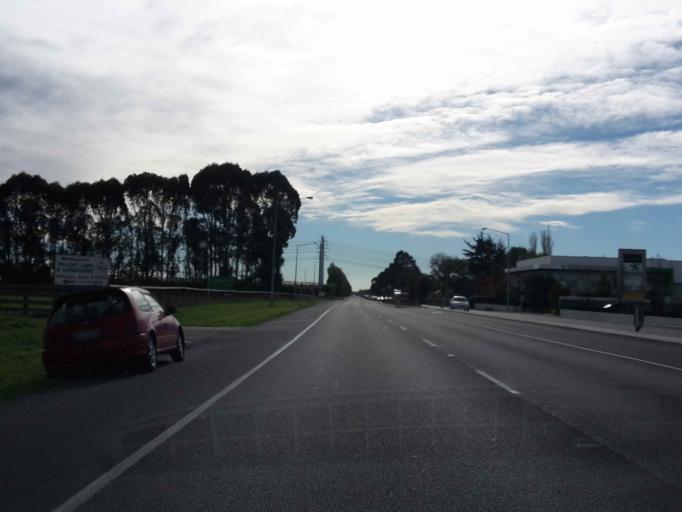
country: NZ
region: Canterbury
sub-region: Selwyn District
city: Prebbleton
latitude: -43.5149
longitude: 172.5372
